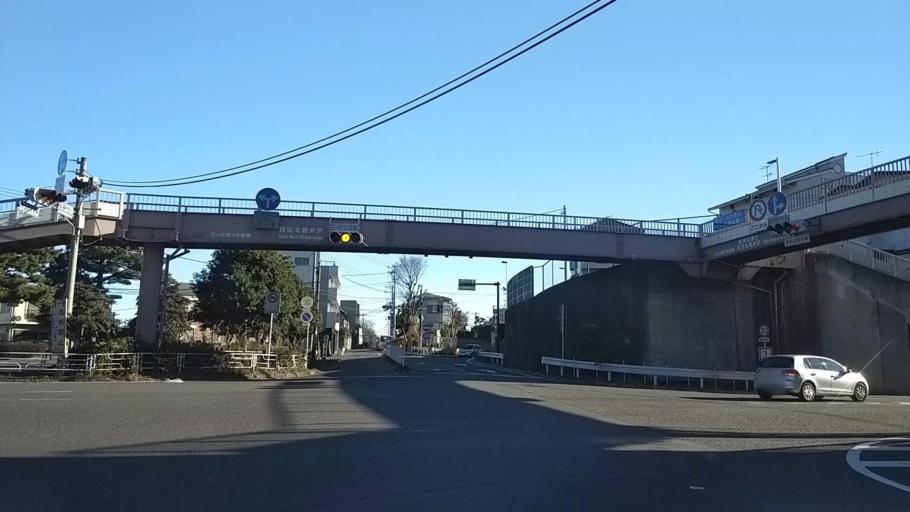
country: JP
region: Kanagawa
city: Yokohama
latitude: 35.4704
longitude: 139.6067
